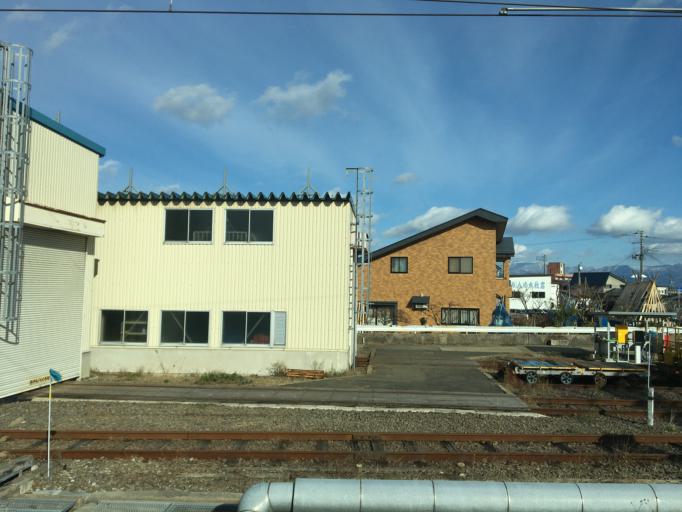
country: JP
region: Akita
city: Omagari
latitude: 39.4674
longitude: 140.4779
